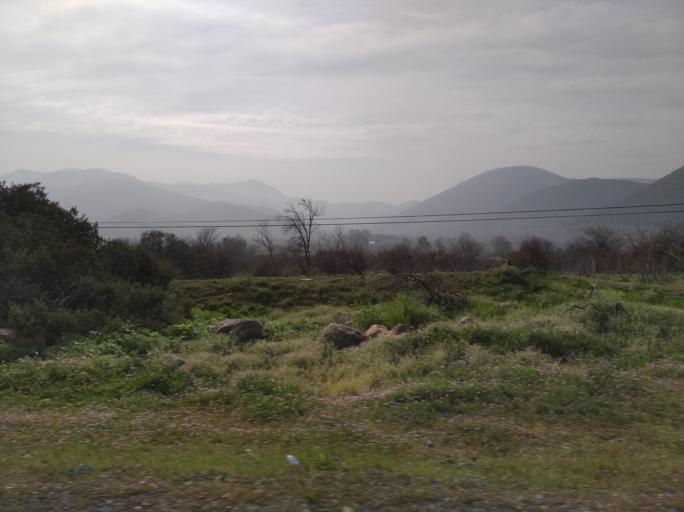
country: CL
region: Santiago Metropolitan
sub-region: Provincia de Chacabuco
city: Lampa
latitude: -33.1314
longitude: -70.9207
